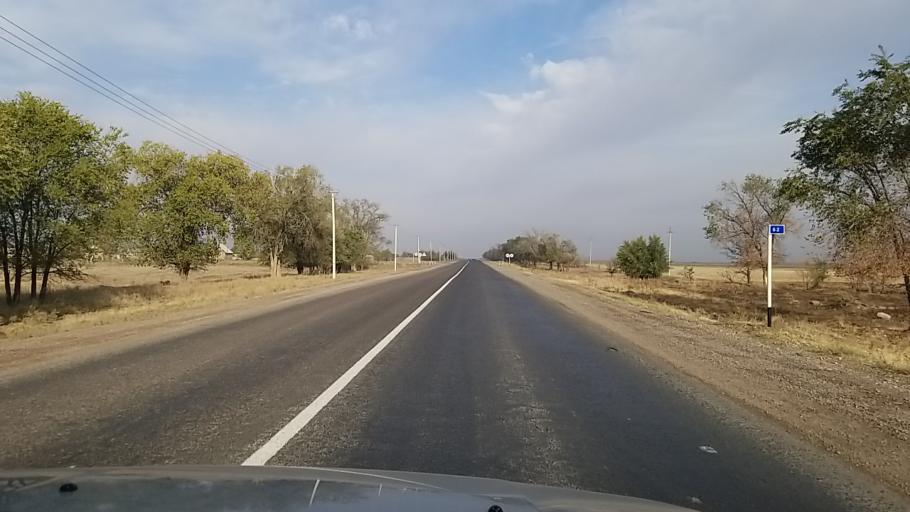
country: KZ
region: Almaty Oblysy
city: Burunday
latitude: 43.4794
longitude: 76.6787
